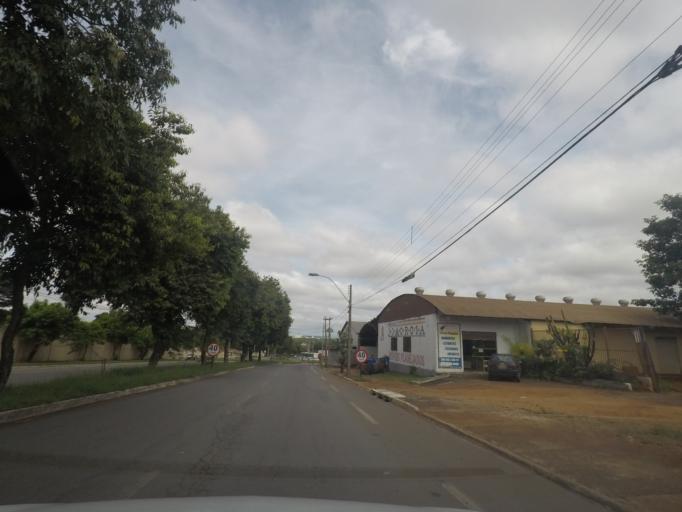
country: BR
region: Goias
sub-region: Goiania
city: Goiania
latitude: -16.6575
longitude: -49.2012
